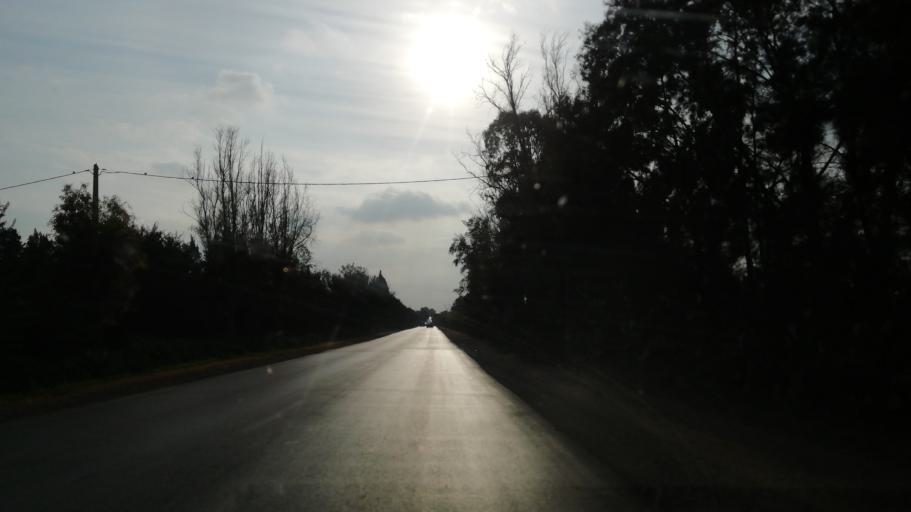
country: DZ
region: Mostaganem
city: Mostaganem
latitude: 35.8381
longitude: 0.0614
